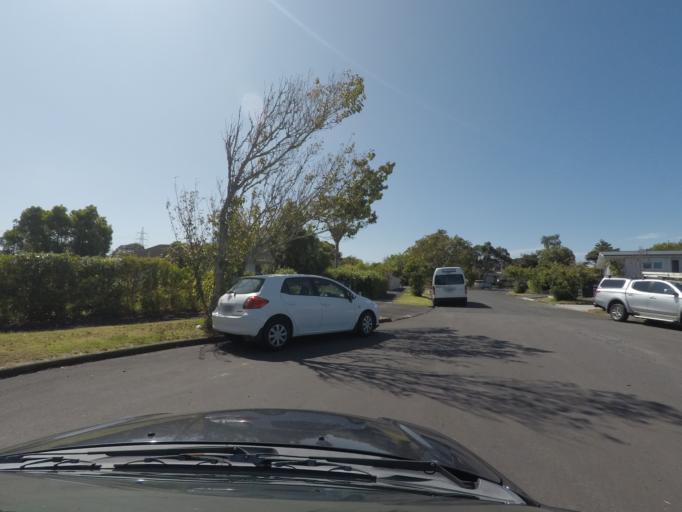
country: NZ
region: Auckland
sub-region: Auckland
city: Rosebank
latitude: -36.8910
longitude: 174.6764
